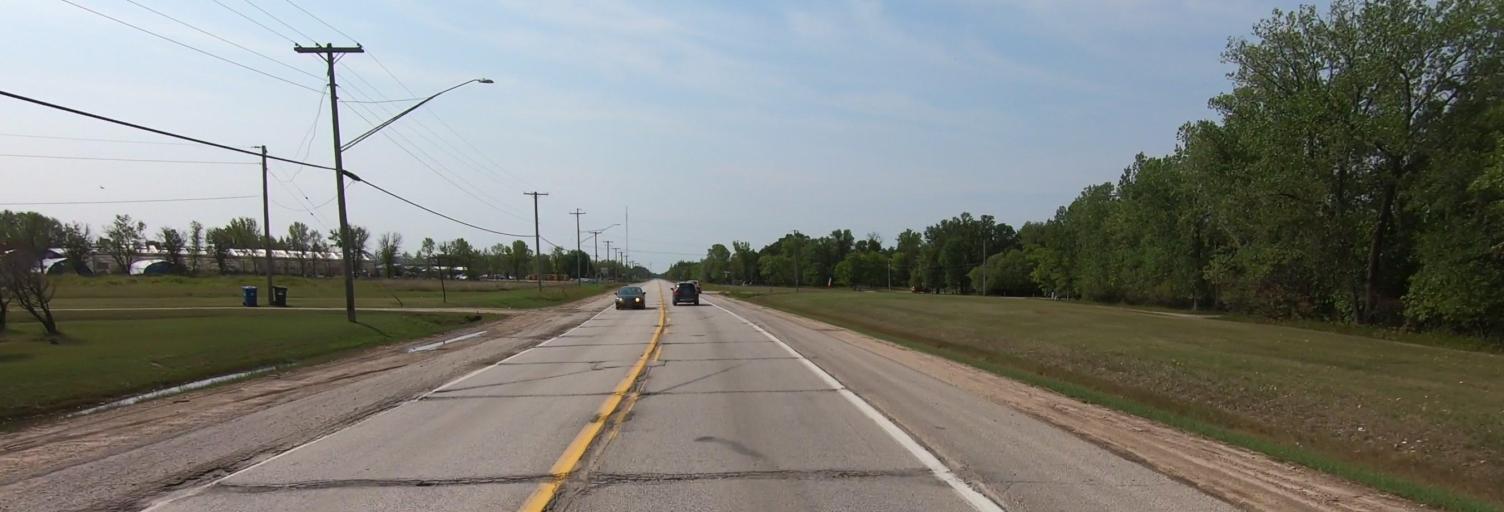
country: CA
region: Manitoba
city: Winnipeg
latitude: 49.7807
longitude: -97.1248
